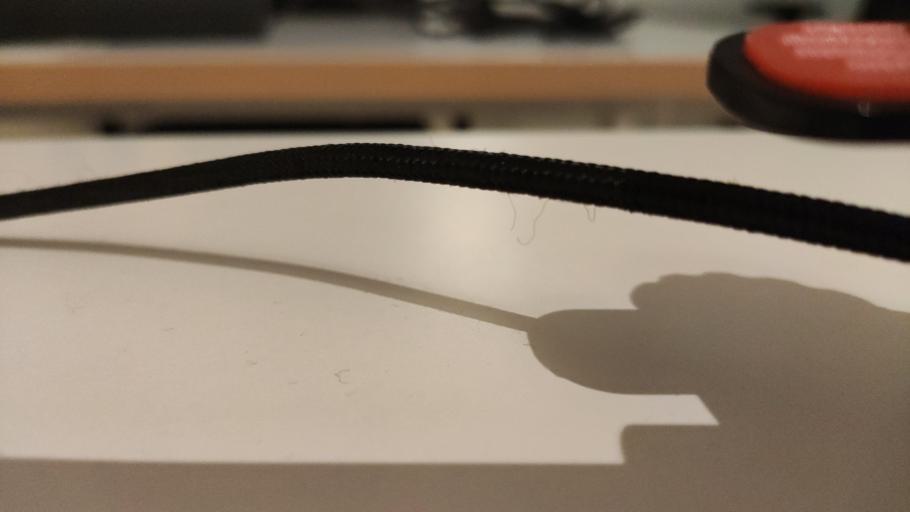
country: RU
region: Moskovskaya
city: Il'inskiy Pogost
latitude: 55.5325
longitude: 38.8725
